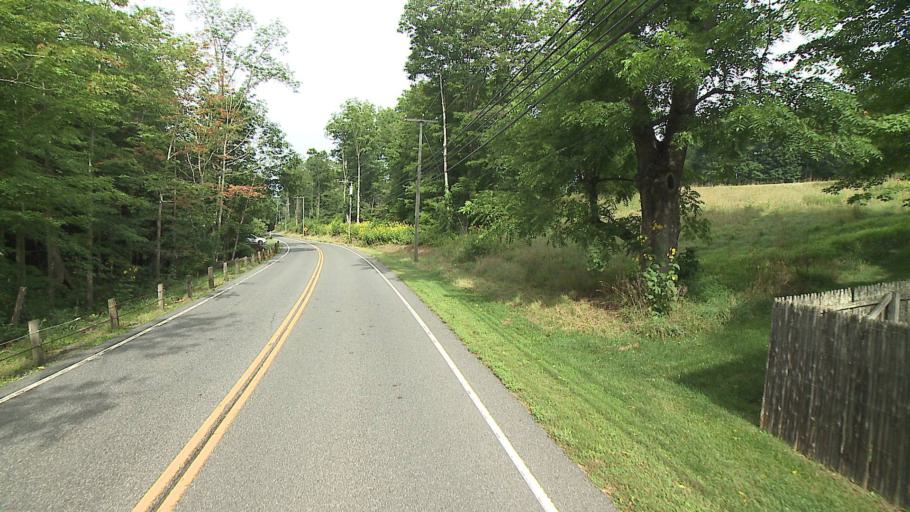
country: US
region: Connecticut
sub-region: Litchfield County
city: New Preston
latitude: 41.6243
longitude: -73.3009
